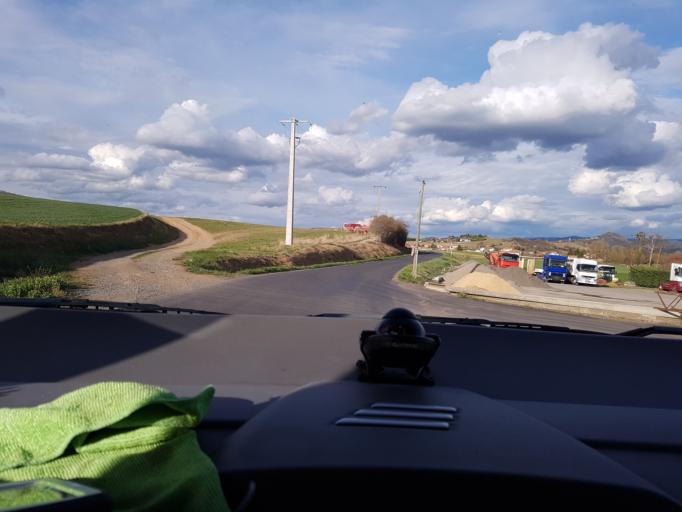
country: FR
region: Auvergne
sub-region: Departement du Puy-de-Dome
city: Saint-Germain-Lembron
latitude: 45.4607
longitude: 3.2240
